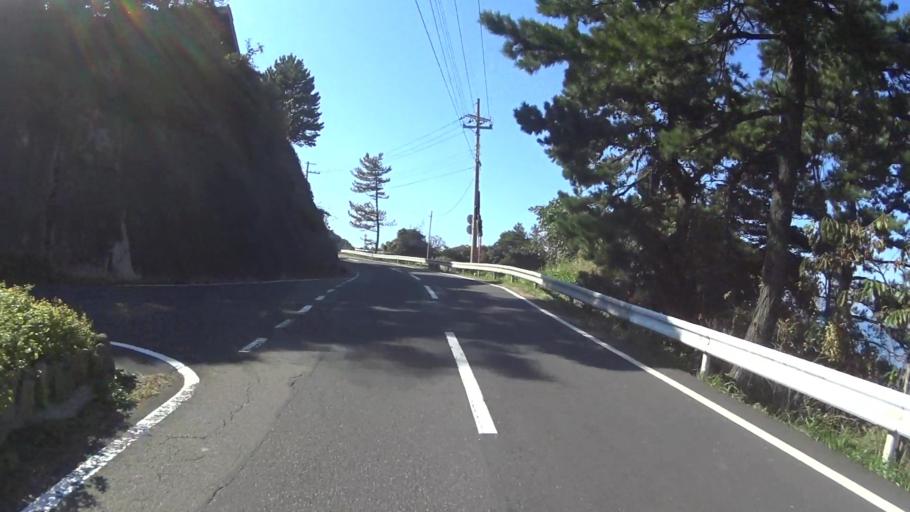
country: JP
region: Kyoto
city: Miyazu
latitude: 35.7640
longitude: 135.2018
